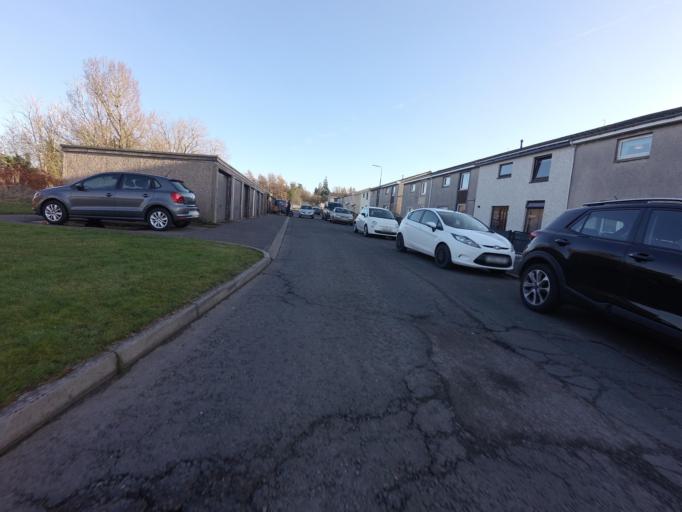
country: GB
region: Scotland
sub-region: West Lothian
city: West Calder
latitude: 55.8648
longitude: -3.5470
